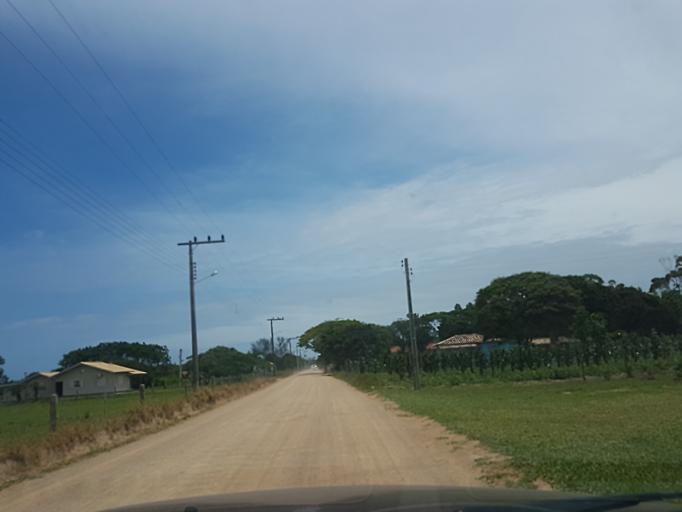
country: BR
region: Santa Catarina
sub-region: Jaguaruna
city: Jaguaruna
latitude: -28.6415
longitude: -48.9637
